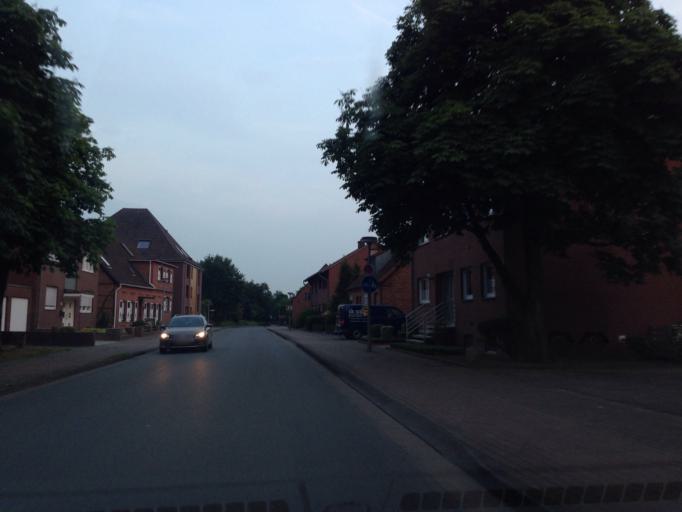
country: DE
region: North Rhine-Westphalia
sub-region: Regierungsbezirk Munster
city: Senden
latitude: 51.8605
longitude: 7.4812
